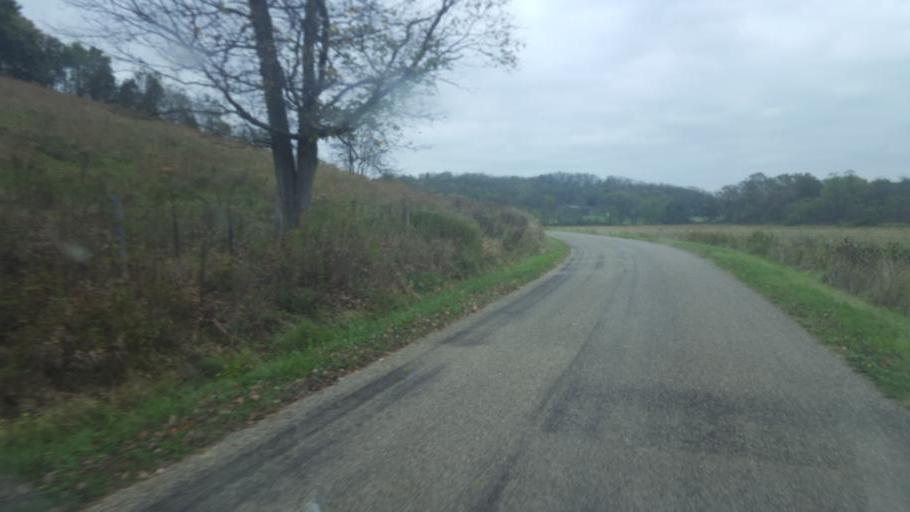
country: US
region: Ohio
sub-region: Carroll County
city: Carrollton
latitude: 40.4296
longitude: -81.0359
